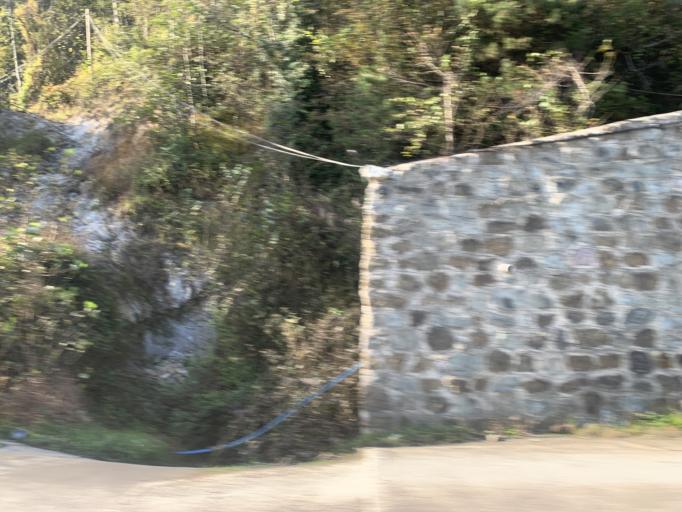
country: TR
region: Trabzon
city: Dernekpazari
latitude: 40.8347
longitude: 40.2714
